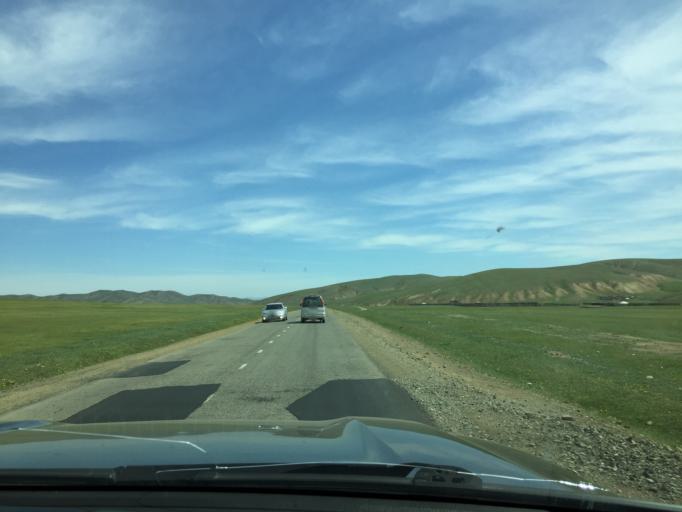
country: MN
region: Central Aimak
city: Bornuur
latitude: 48.6651
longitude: 106.1289
